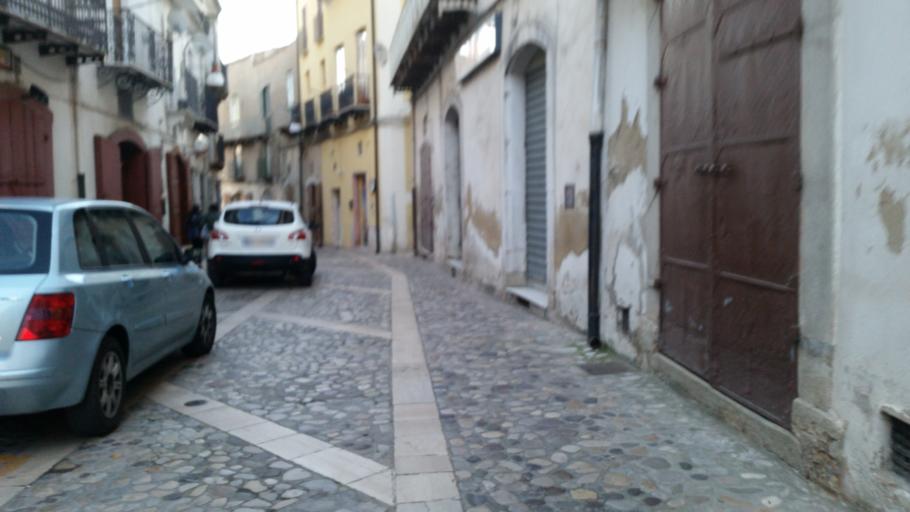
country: IT
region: Basilicate
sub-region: Provincia di Matera
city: Tricarico
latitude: 40.6234
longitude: 16.1442
